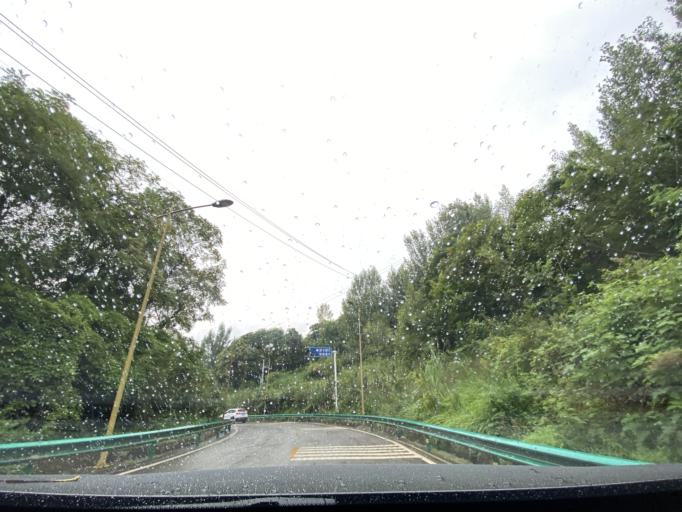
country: CN
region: Sichuan
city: Longquan
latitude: 30.6078
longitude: 104.4835
